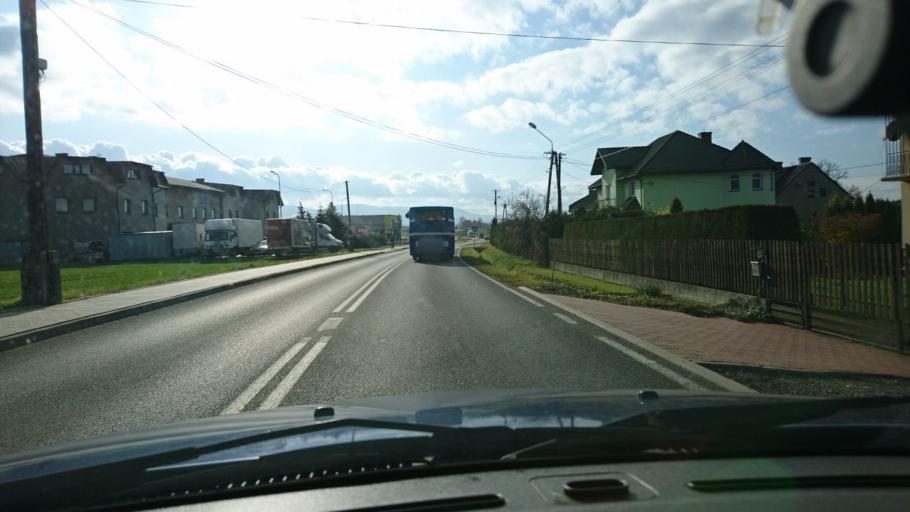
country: PL
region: Silesian Voivodeship
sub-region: Powiat bielski
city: Wilamowice
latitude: 49.9113
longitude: 19.1515
